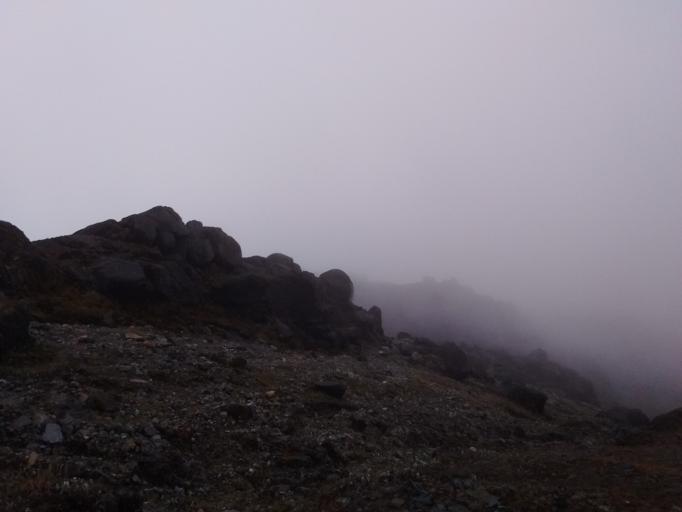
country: CO
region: Cauca
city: Totoro
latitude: 2.3254
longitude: -76.3946
